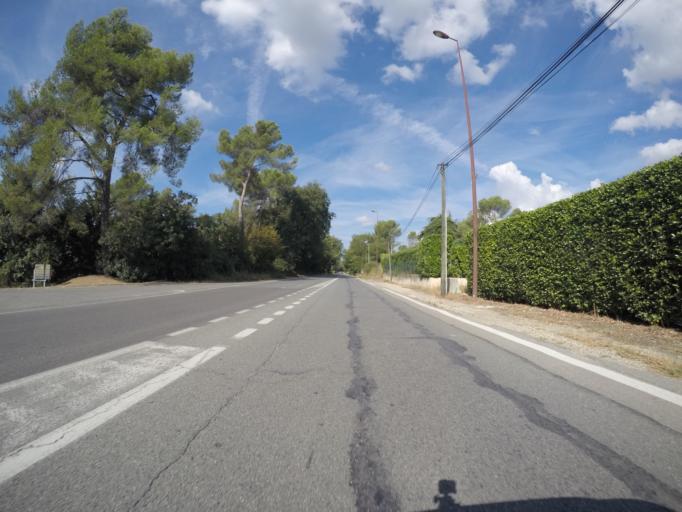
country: FR
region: Provence-Alpes-Cote d'Azur
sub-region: Departement des Alpes-Maritimes
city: Le Rouret
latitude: 43.6722
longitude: 7.0362
